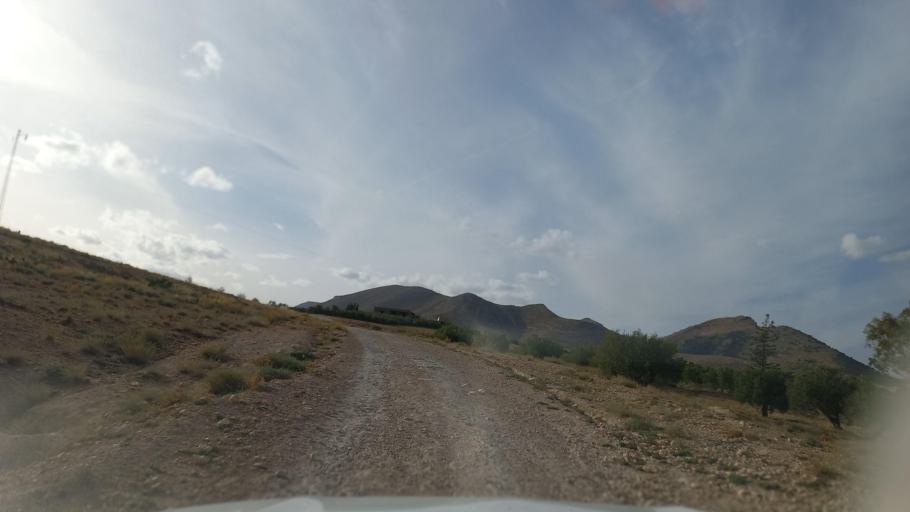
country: TN
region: Al Qasrayn
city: Sbiba
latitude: 35.4537
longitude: 9.0830
